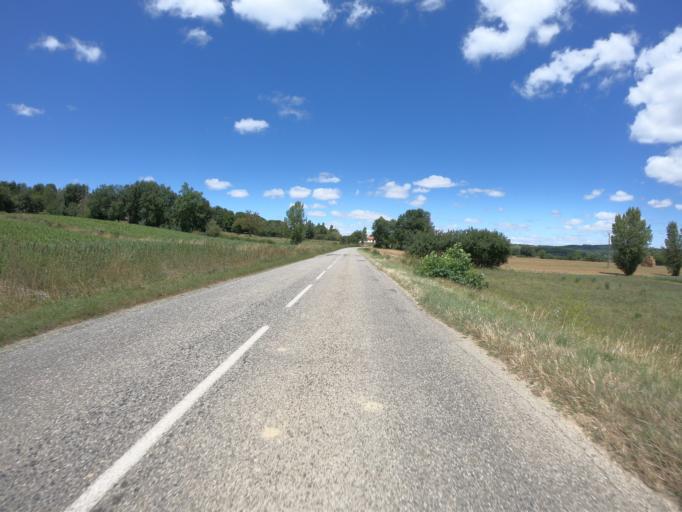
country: FR
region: Midi-Pyrenees
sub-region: Departement de l'Ariege
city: Verniolle
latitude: 43.0763
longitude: 1.7392
